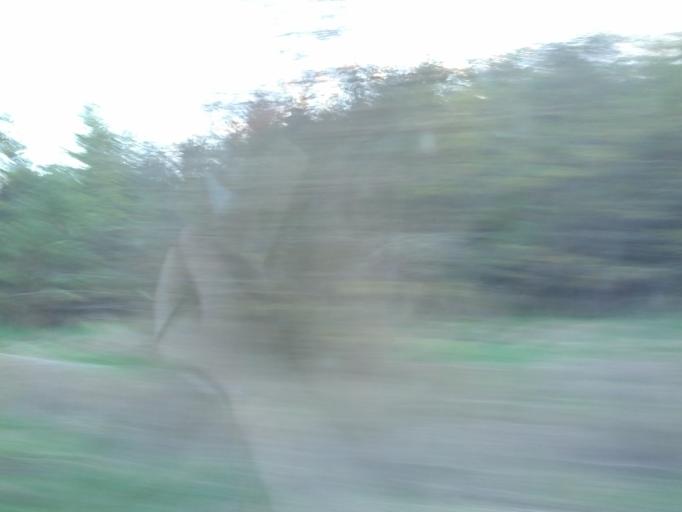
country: IE
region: Connaught
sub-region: County Galway
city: Athenry
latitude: 53.3366
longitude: -8.7044
